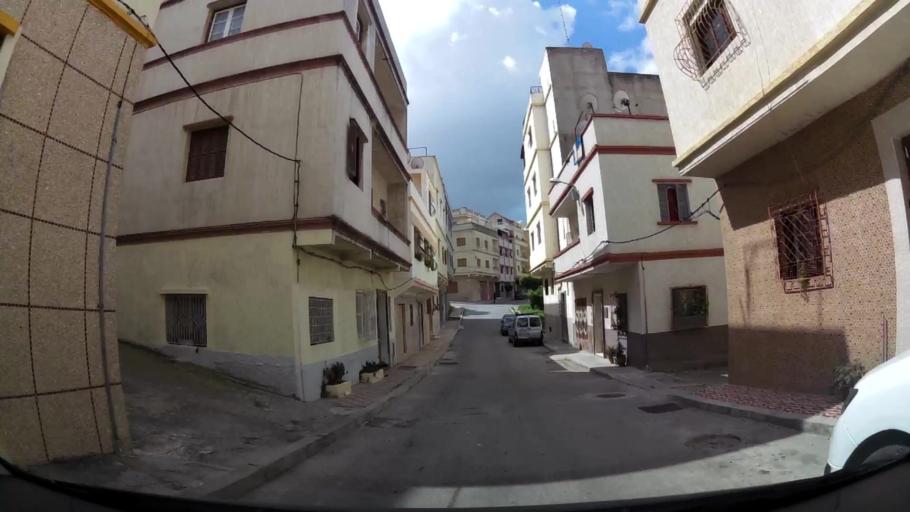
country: MA
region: Tanger-Tetouan
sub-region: Tanger-Assilah
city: Tangier
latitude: 35.7609
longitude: -5.8144
